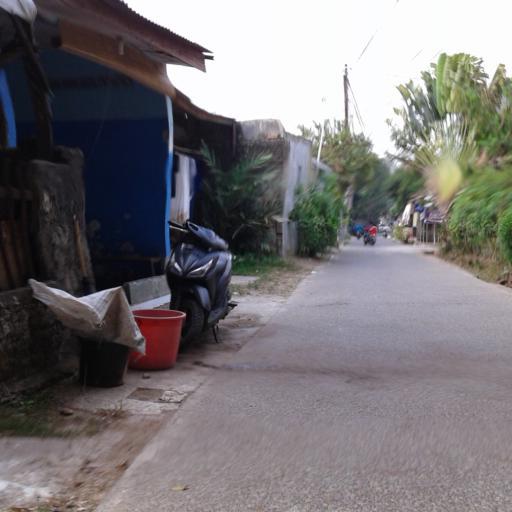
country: ID
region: West Java
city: Sawangan
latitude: -6.4008
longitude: 106.7659
